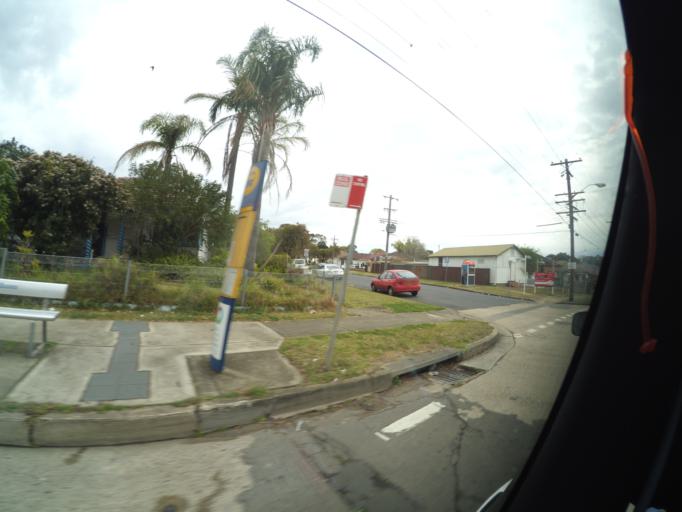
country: AU
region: New South Wales
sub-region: Bankstown
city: Bankstown
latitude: -33.9299
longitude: 151.0298
